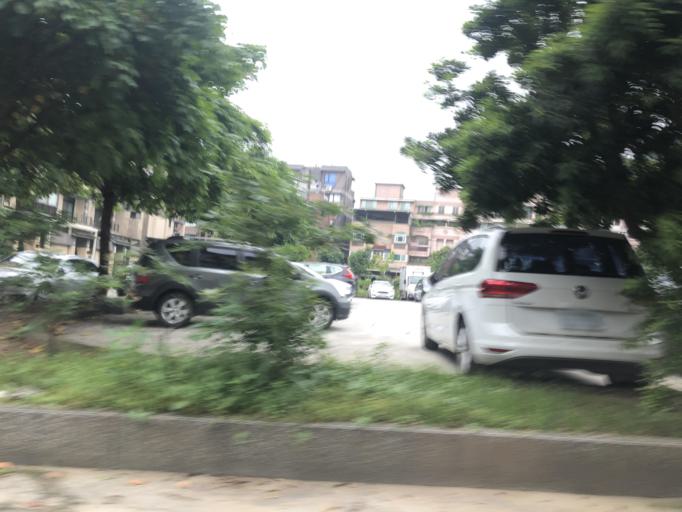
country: TW
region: Taiwan
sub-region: Keelung
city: Keelung
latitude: 25.1591
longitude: 121.6968
